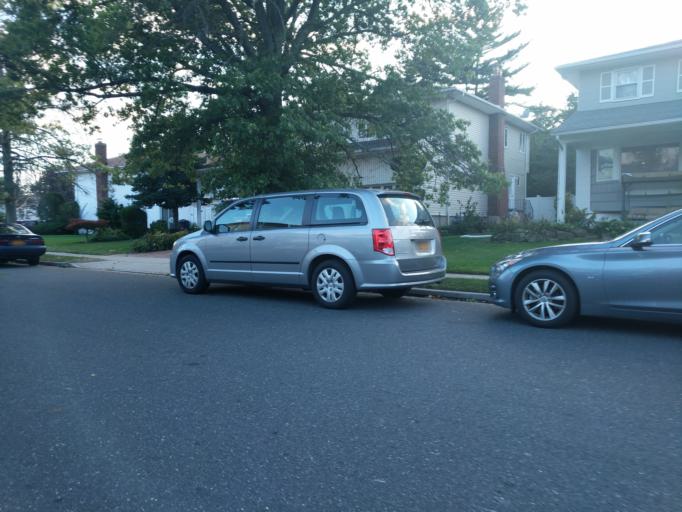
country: US
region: New York
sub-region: Nassau County
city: South Valley Stream
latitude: 40.6452
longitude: -73.7300
